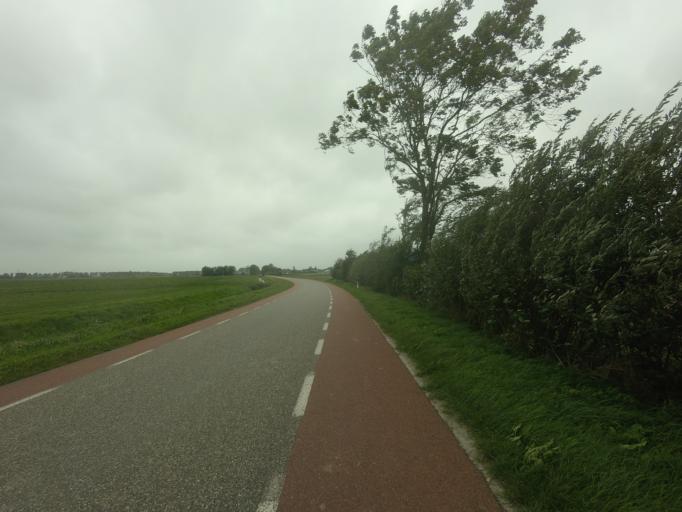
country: NL
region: Friesland
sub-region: Gemeente Ferwerderadiel
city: Ferwert
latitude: 53.3350
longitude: 5.8460
